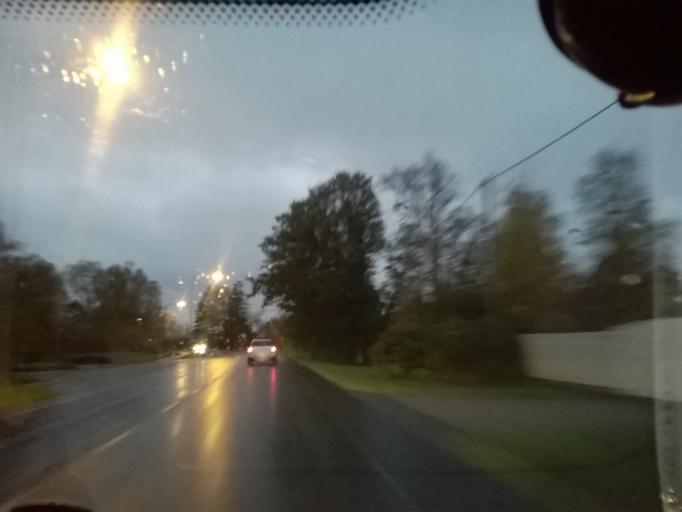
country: EE
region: Harju
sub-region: Viimsi vald
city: Rummu
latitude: 59.5407
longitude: 24.7944
